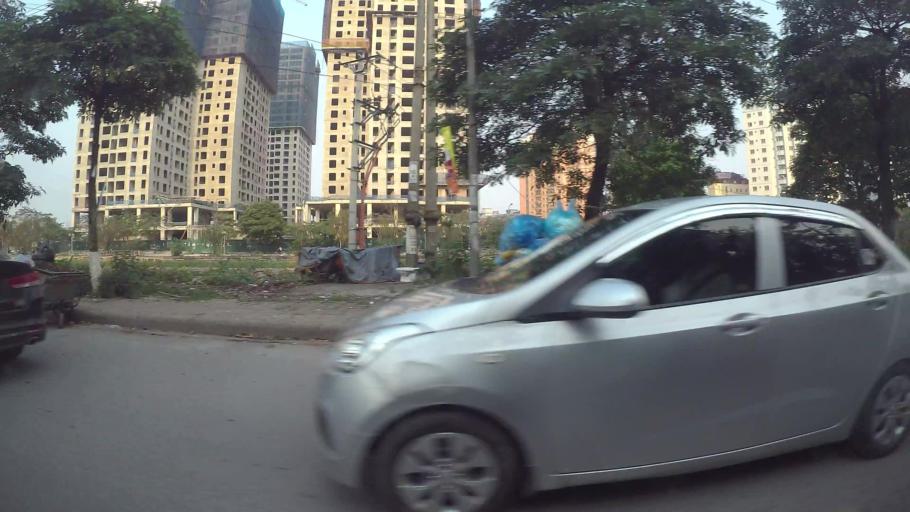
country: VN
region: Ha Noi
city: Thanh Xuan
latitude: 20.9727
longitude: 105.8247
